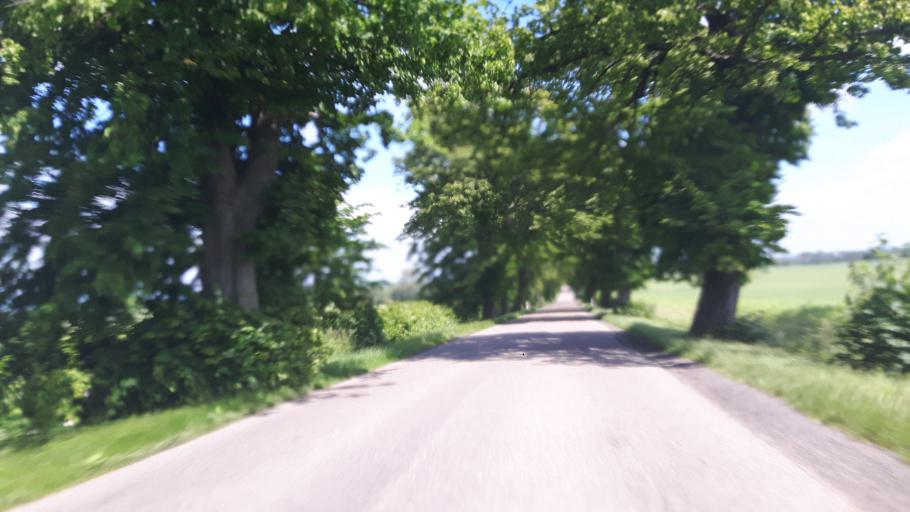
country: PL
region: Pomeranian Voivodeship
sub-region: Powiat slupski
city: Ustka
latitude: 54.5213
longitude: 16.7788
